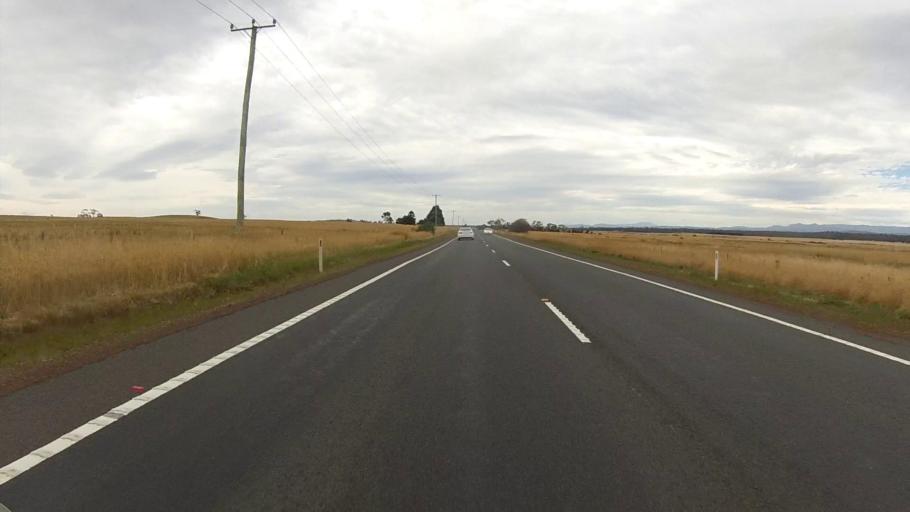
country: AU
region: Tasmania
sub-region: Northern Midlands
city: Evandale
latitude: -41.9006
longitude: 147.4760
